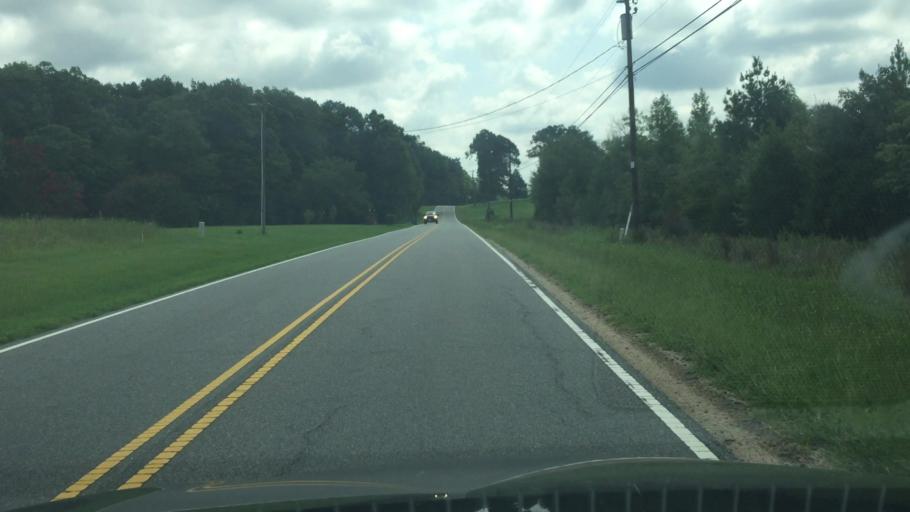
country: US
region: North Carolina
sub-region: Rowan County
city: Enochville
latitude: 35.4869
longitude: -80.7395
